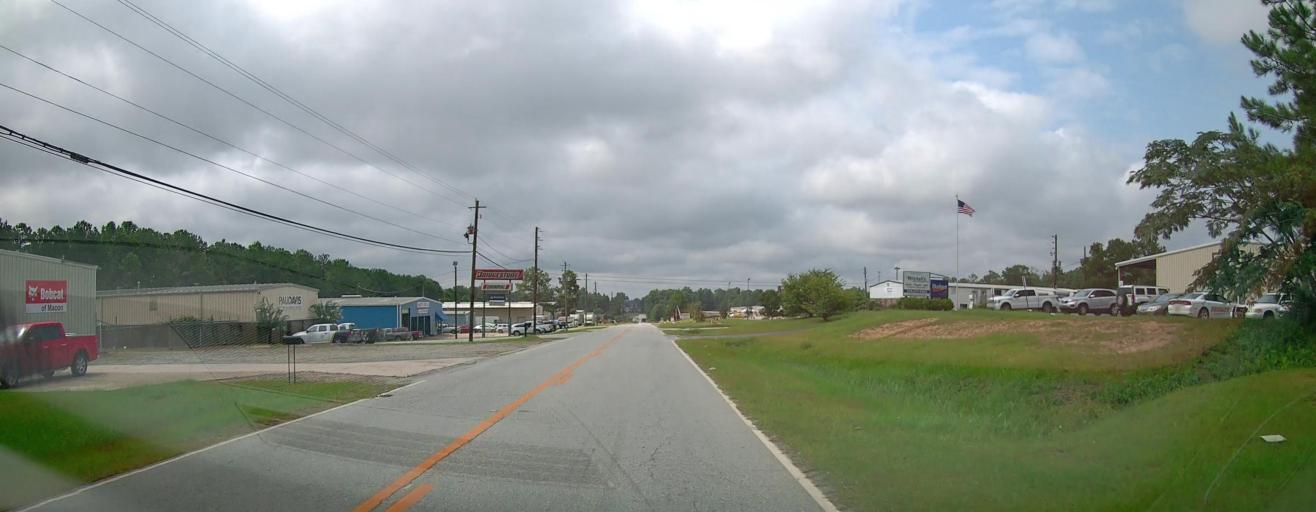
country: US
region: Georgia
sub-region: Bibb County
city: West Point
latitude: 32.8301
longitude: -83.7293
